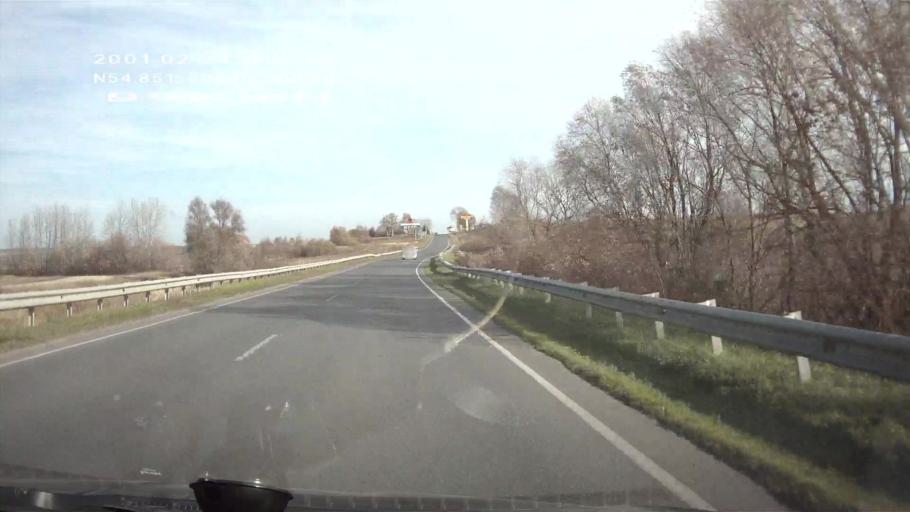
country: RU
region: Mordoviya
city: Turgenevo
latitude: 54.8514
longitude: 46.3896
